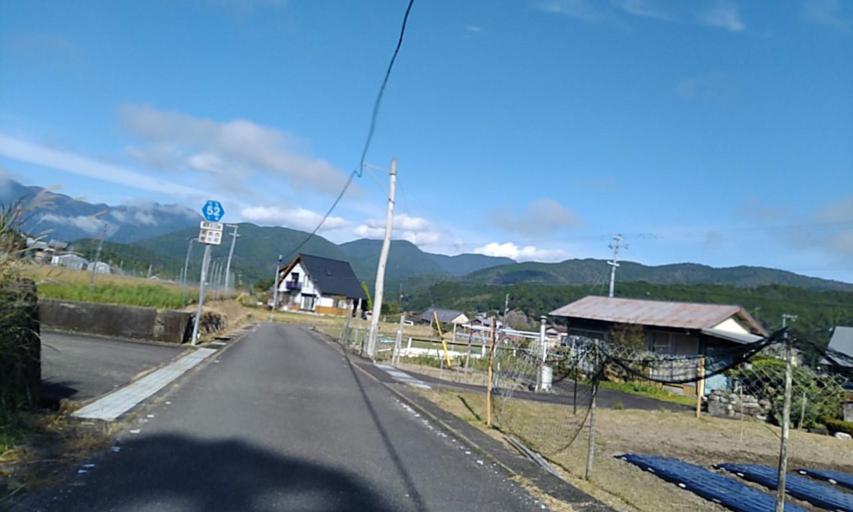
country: JP
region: Wakayama
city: Shingu
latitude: 33.9182
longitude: 135.9877
